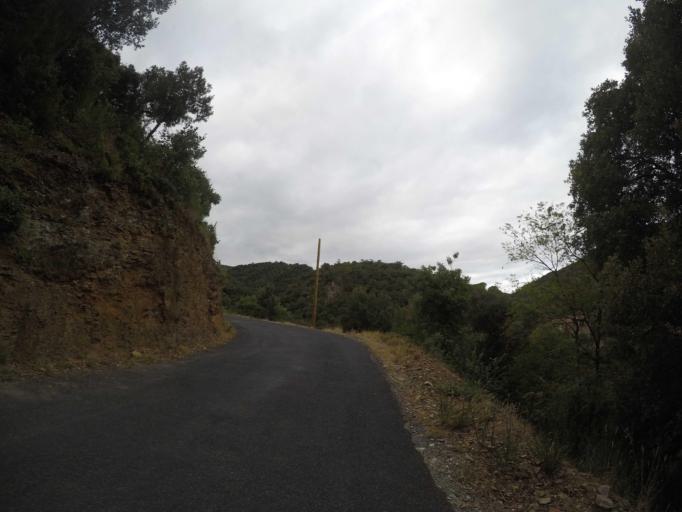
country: FR
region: Languedoc-Roussillon
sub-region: Departement des Pyrenees-Orientales
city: Ille-sur-Tet
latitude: 42.6413
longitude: 2.6223
